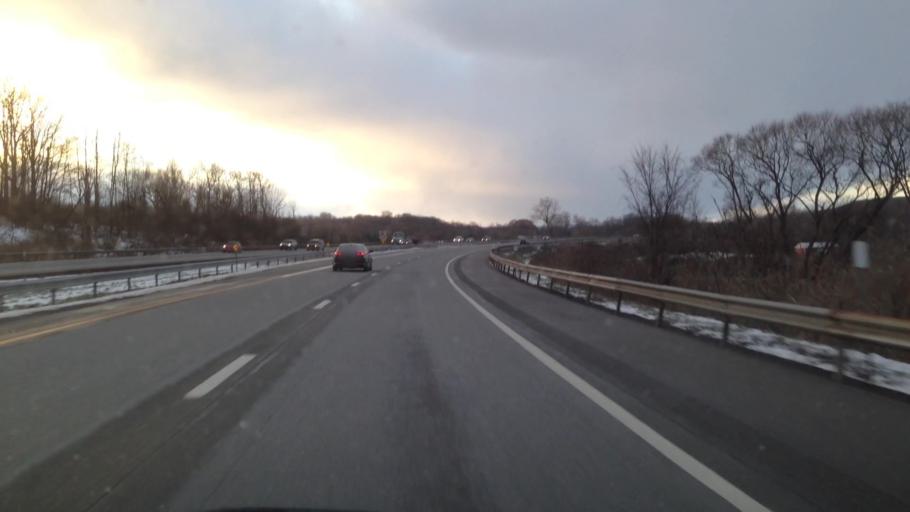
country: US
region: New York
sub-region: Herkimer County
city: Herkimer
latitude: 43.0139
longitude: -74.9705
